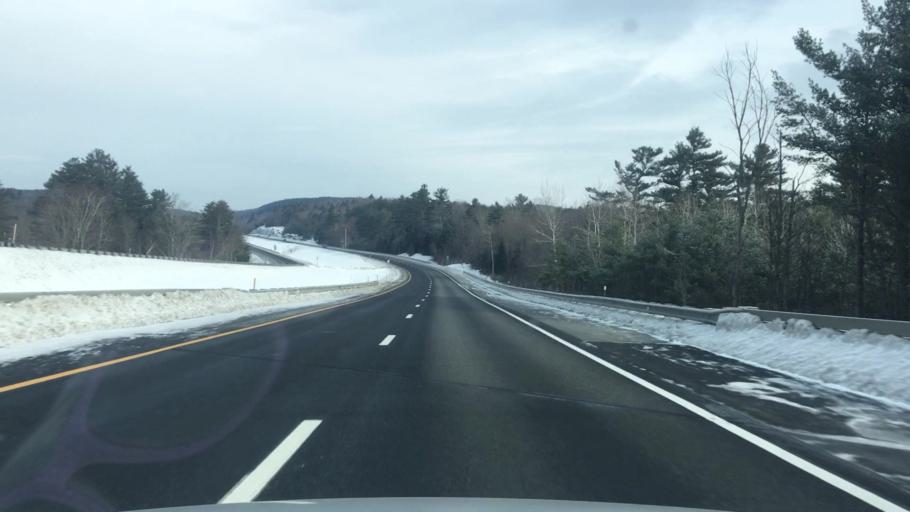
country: US
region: New Hampshire
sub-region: Sullivan County
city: Grantham
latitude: 43.5386
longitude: -72.1384
